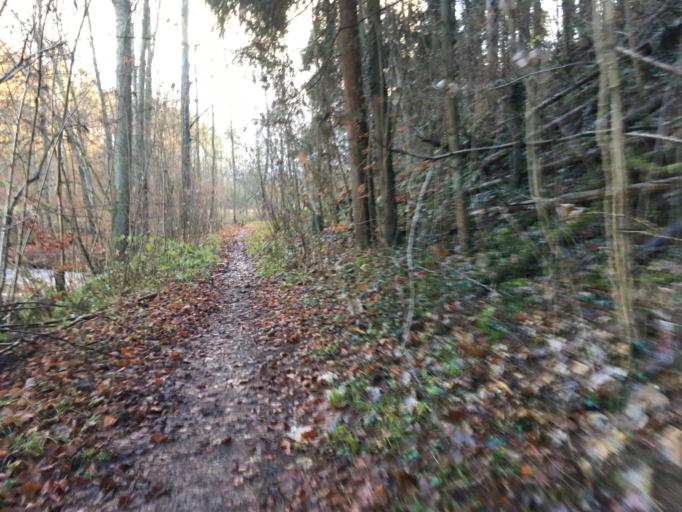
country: DE
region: Baden-Wuerttemberg
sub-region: Regierungsbezirk Stuttgart
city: Talheim
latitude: 49.0734
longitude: 9.2000
